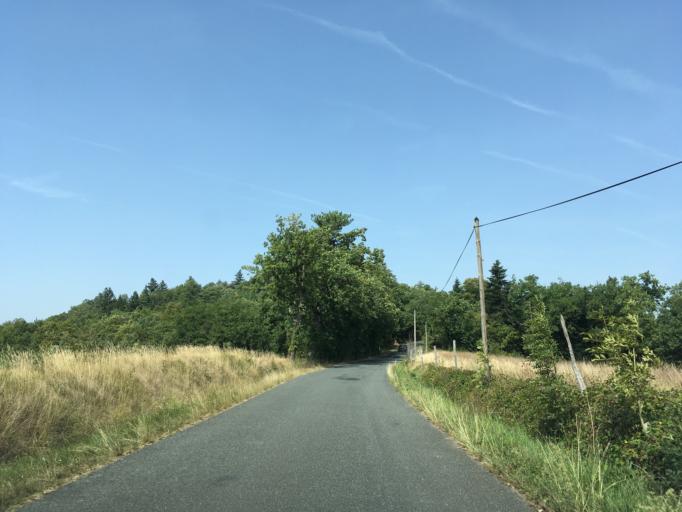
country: FR
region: Midi-Pyrenees
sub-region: Departement du Tarn
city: Lagarrigue
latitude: 43.5941
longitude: 2.3097
